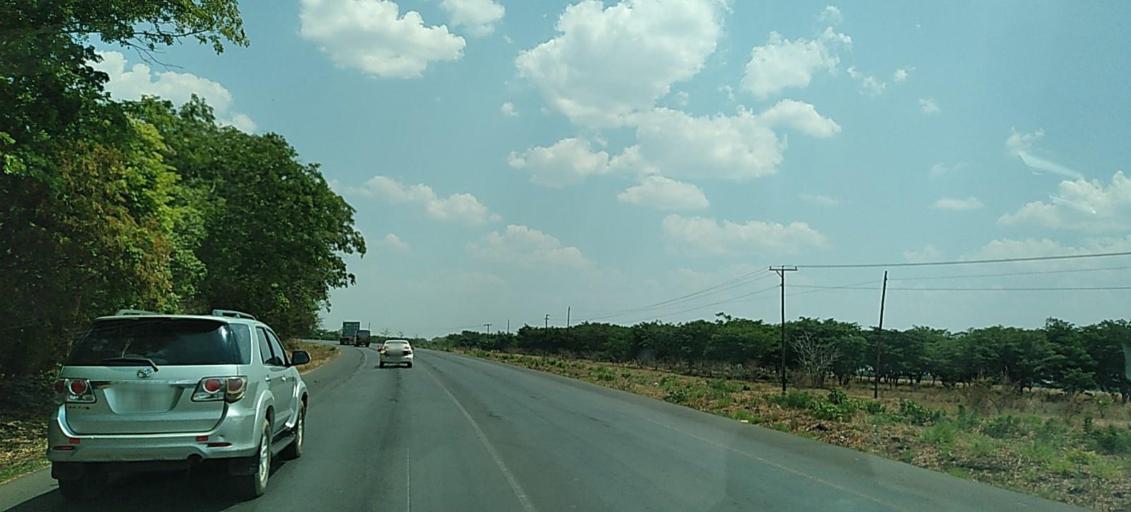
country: ZM
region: Central
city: Kabwe
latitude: -14.3071
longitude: 28.5451
